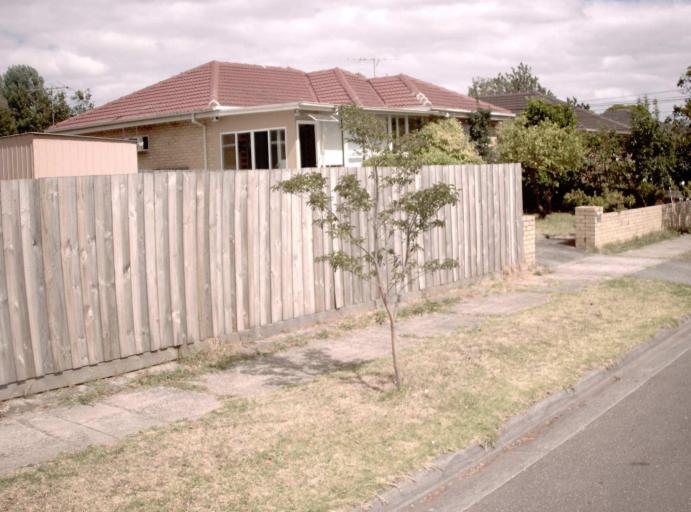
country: AU
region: Victoria
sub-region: Greater Dandenong
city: Springvale
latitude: -37.9338
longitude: 145.1596
